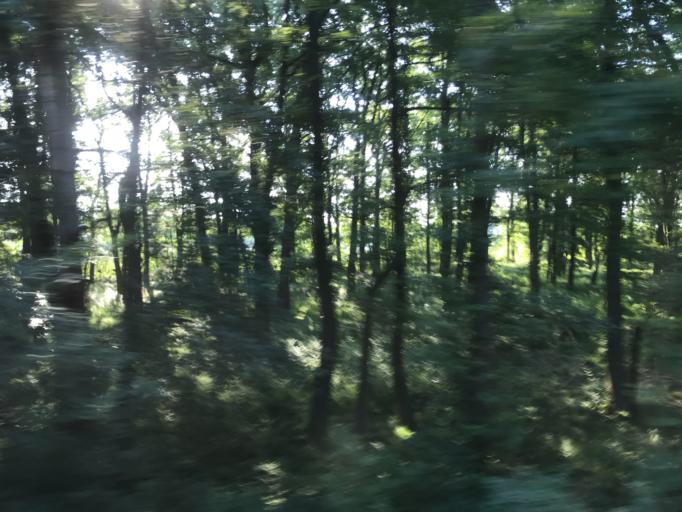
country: CZ
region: Jihocesky
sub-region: Okres Jindrichuv Hradec
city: Lomnice nad Luznici
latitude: 49.1242
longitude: 14.7387
